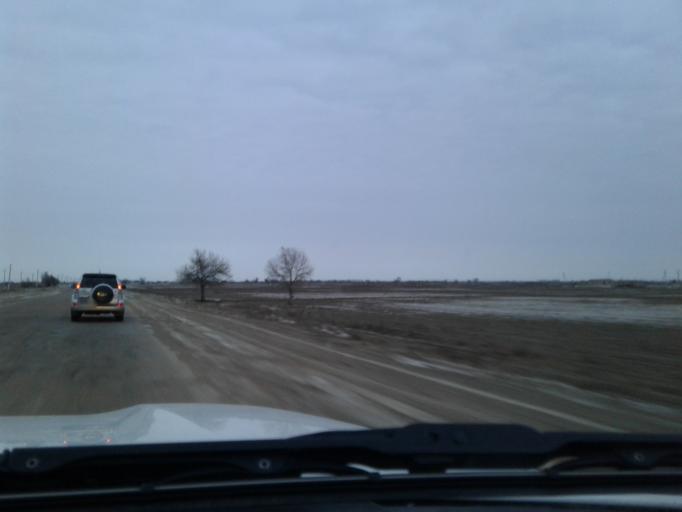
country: UZ
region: Karakalpakstan
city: Manghit
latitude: 42.0182
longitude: 59.8970
